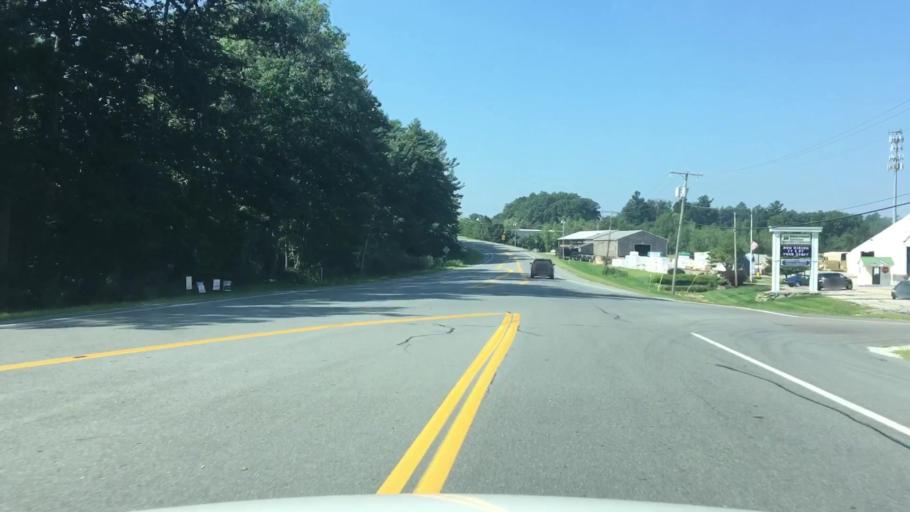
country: US
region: New Hampshire
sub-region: Rockingham County
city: Danville
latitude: 42.8904
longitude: -71.1437
